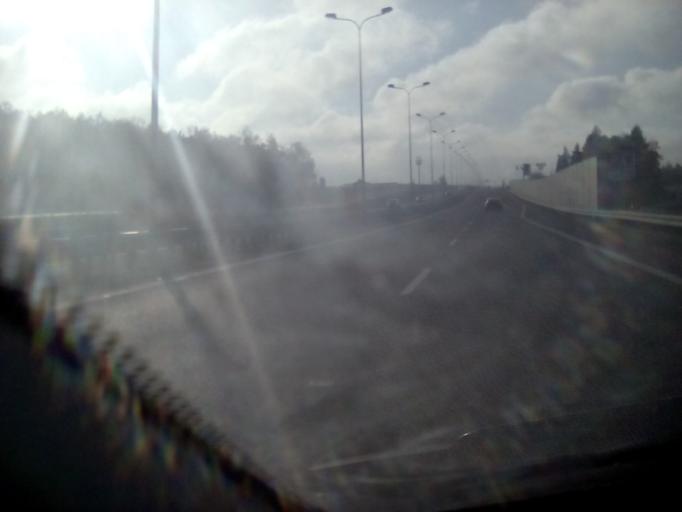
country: PL
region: Masovian Voivodeship
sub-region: Powiat grojecki
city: Goszczyn
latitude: 51.7504
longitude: 20.9083
